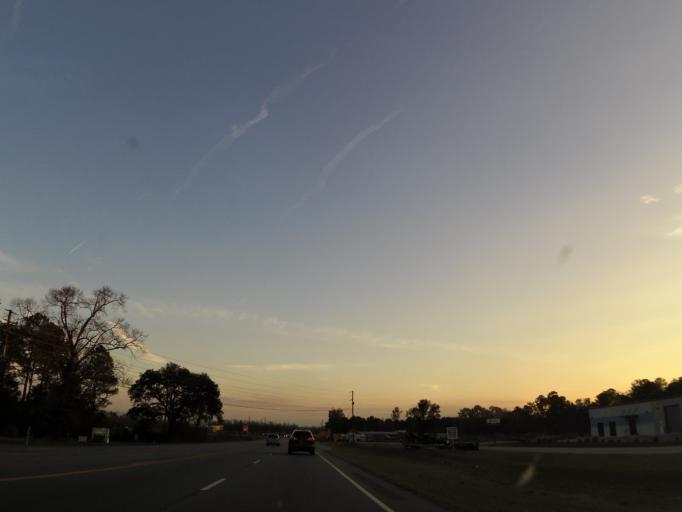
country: US
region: Georgia
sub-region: Lee County
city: Leesburg
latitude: 31.6612
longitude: -84.1729
